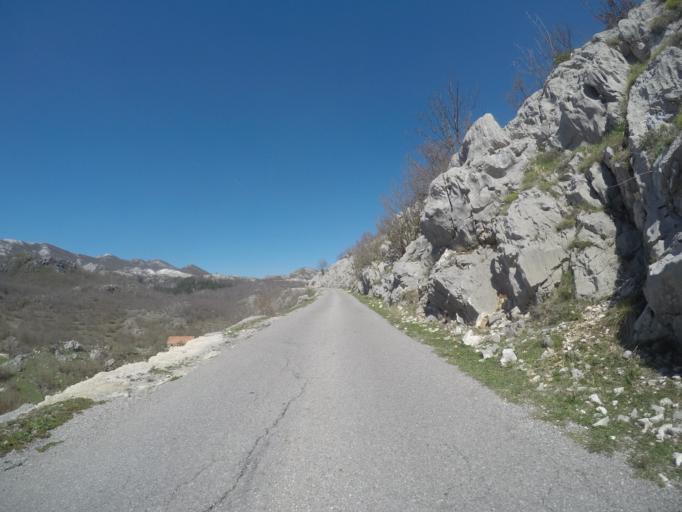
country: ME
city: Dobrota
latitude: 42.4711
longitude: 18.8587
